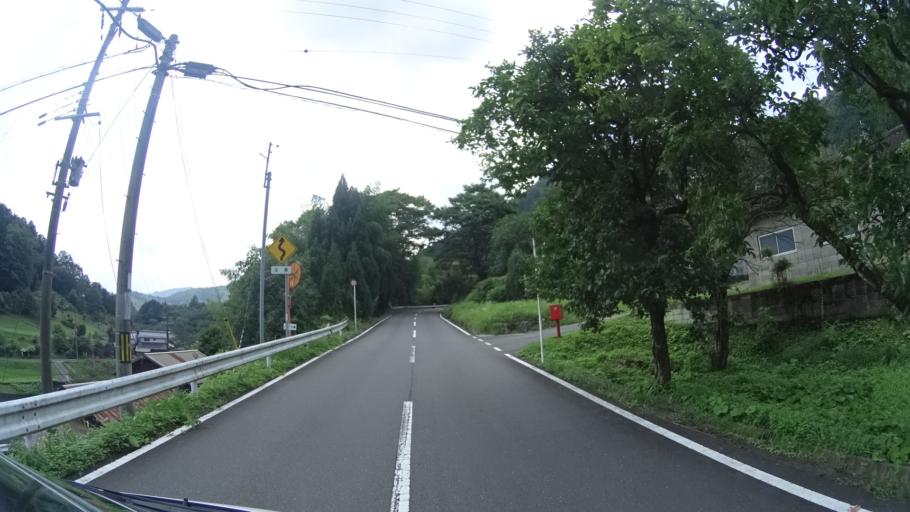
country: JP
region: Kyoto
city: Ayabe
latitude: 35.1901
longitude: 135.2649
